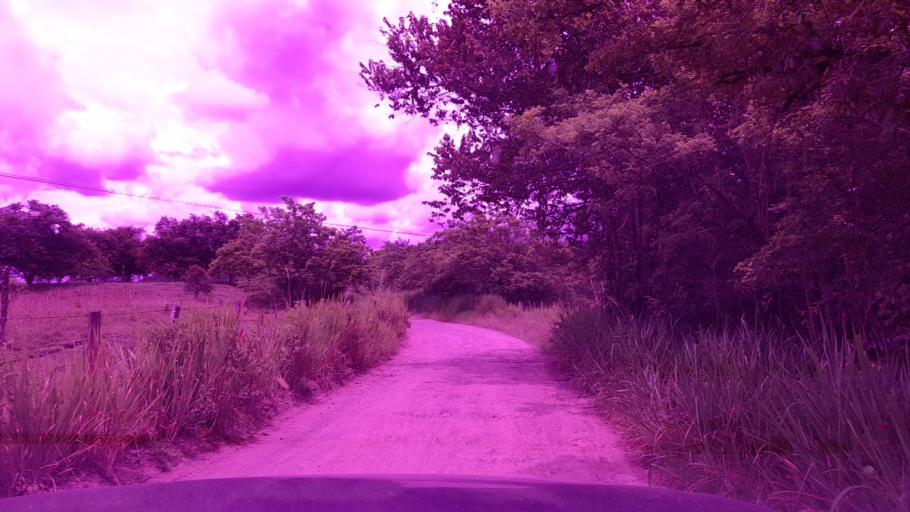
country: CO
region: Valle del Cauca
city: Andalucia
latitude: 4.1788
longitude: -76.1345
